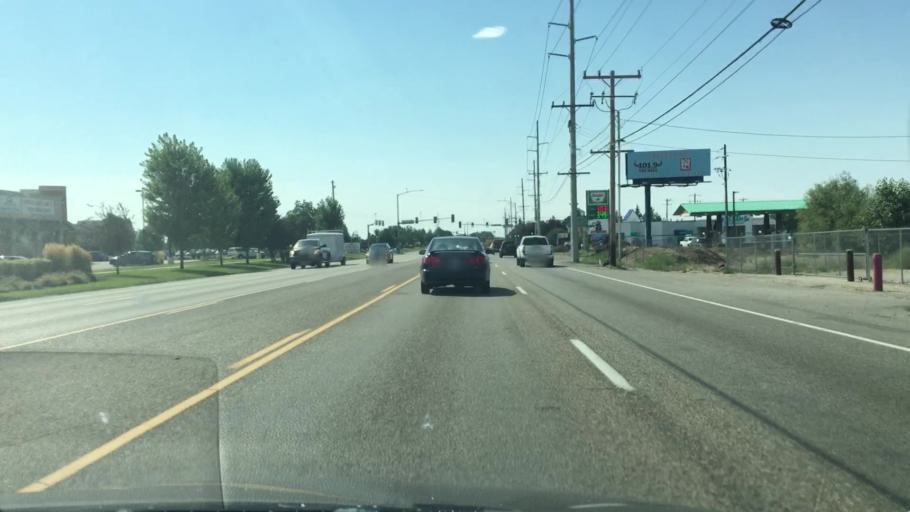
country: US
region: Idaho
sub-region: Ada County
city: Eagle
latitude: 43.6819
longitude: -116.3119
